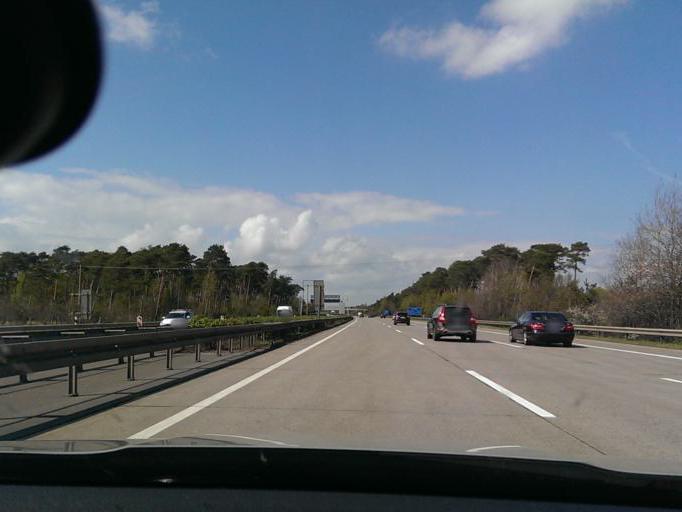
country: DE
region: Lower Saxony
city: Elze
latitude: 52.5663
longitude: 9.7855
